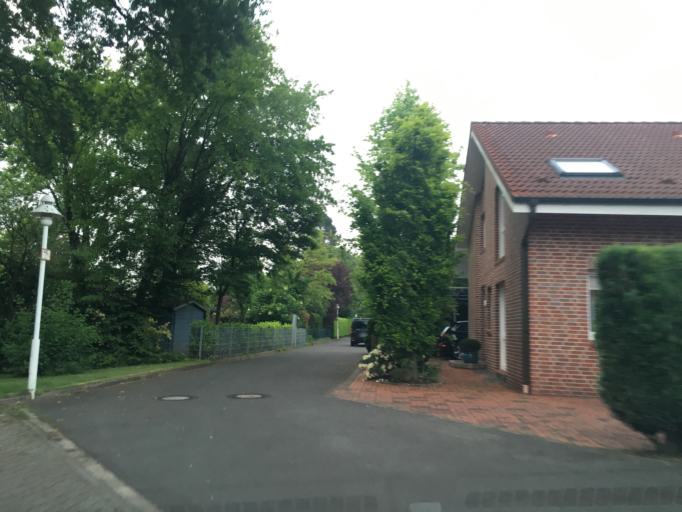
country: DE
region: North Rhine-Westphalia
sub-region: Regierungsbezirk Munster
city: Muenster
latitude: 51.9939
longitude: 7.5615
